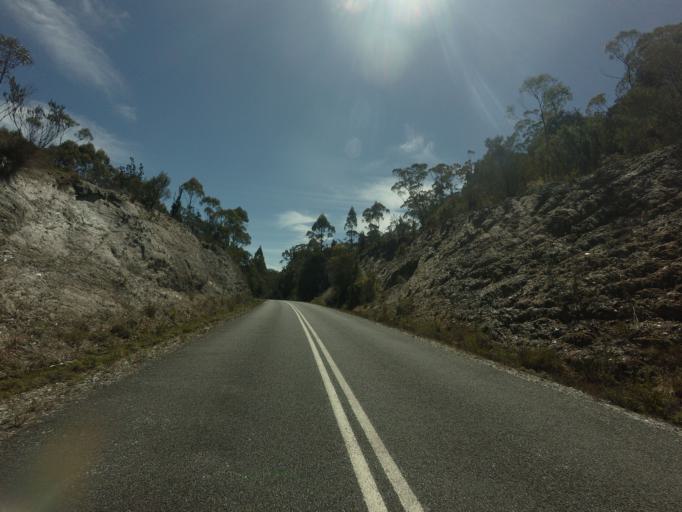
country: AU
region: Tasmania
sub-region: West Coast
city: Queenstown
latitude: -42.7739
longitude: 146.0279
